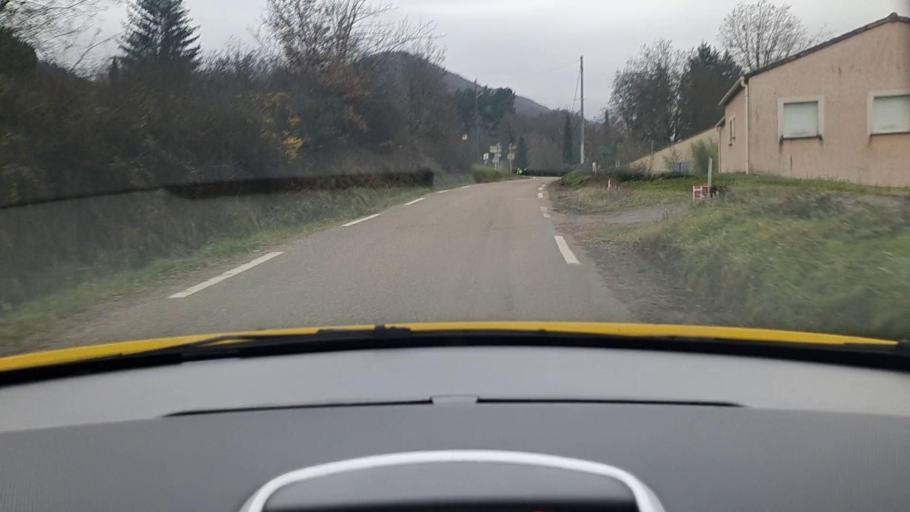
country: FR
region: Languedoc-Roussillon
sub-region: Departement du Gard
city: Besseges
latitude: 44.3183
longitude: 4.1327
